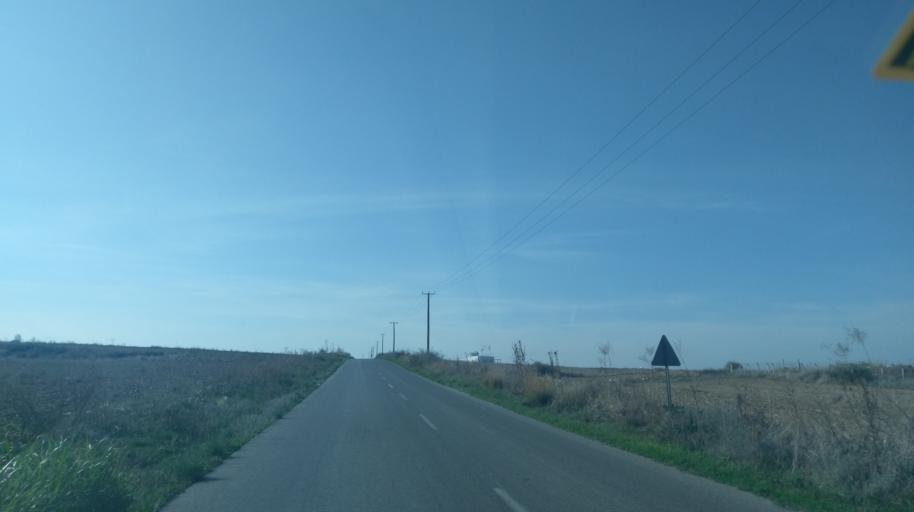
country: CY
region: Larnaka
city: Athienou
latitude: 35.1610
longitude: 33.5149
